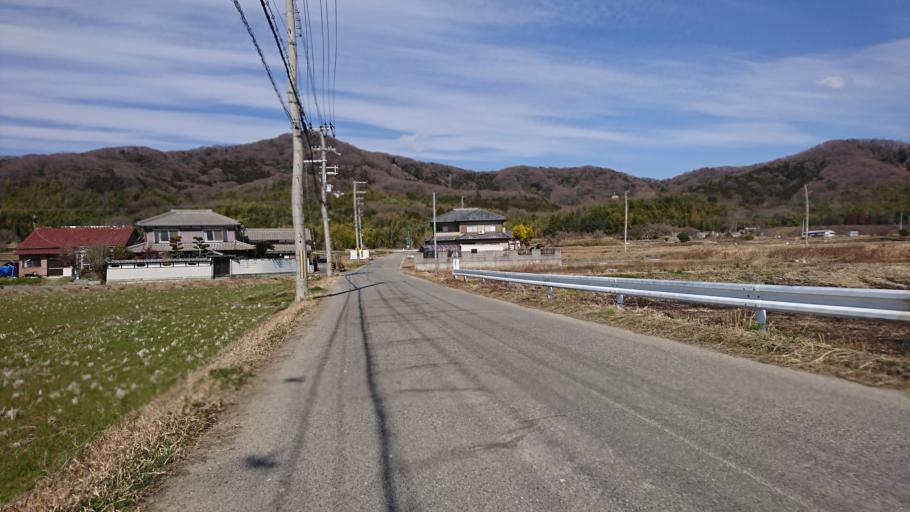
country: JP
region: Hyogo
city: Kakogawacho-honmachi
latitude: 34.8252
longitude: 134.8061
